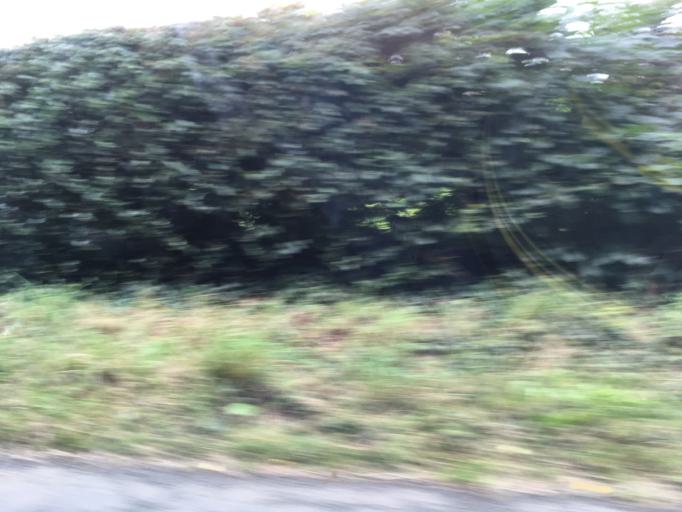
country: IE
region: Leinster
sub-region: Wicklow
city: Wicklow
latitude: 52.9164
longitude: -6.0920
